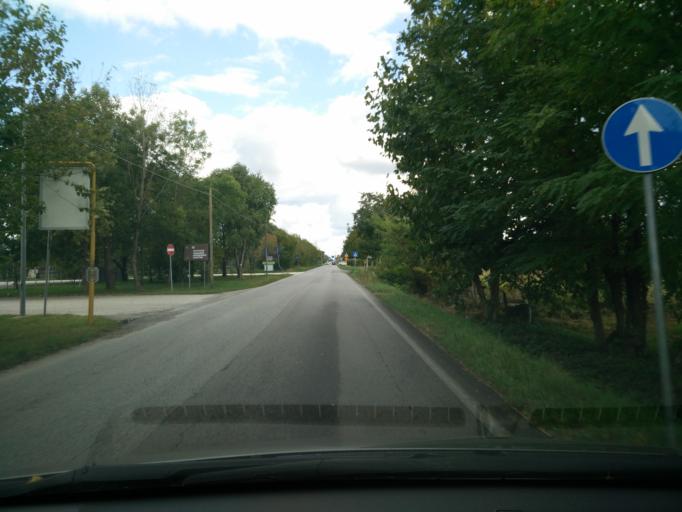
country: IT
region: Veneto
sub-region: Provincia di Treviso
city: Castelfranco Veneto
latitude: 45.6908
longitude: 11.9467
